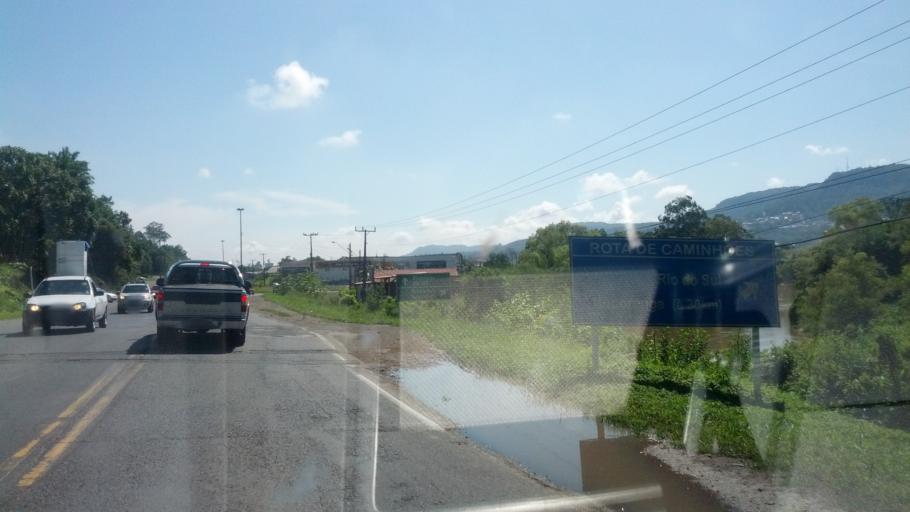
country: BR
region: Santa Catarina
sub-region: Rio Do Sul
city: Rio do Sul
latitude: -27.2223
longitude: -49.6624
